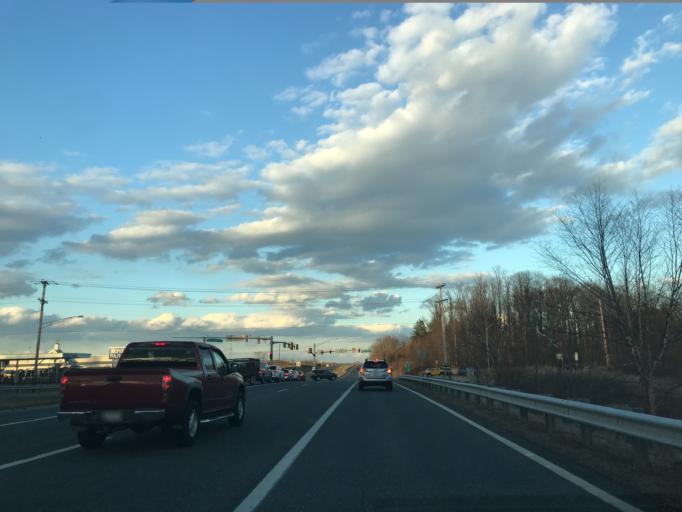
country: US
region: Maryland
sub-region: Harford County
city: Bel Air North
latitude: 39.5747
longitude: -76.3438
